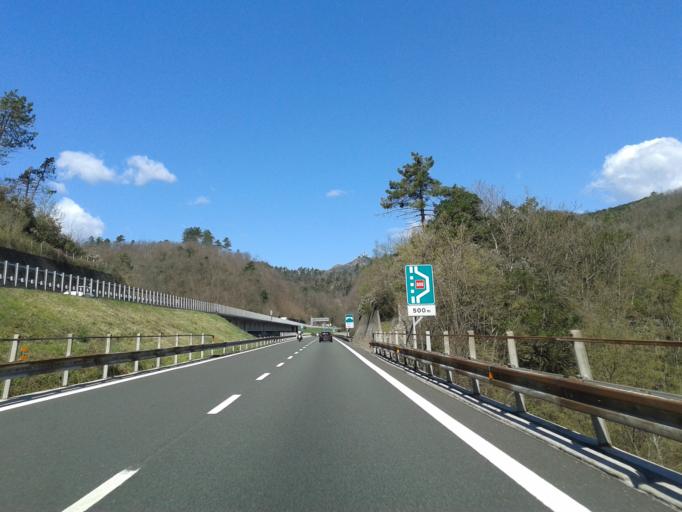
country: IT
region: Liguria
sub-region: Provincia di La Spezia
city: Carrodano
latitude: 44.2297
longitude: 9.6084
